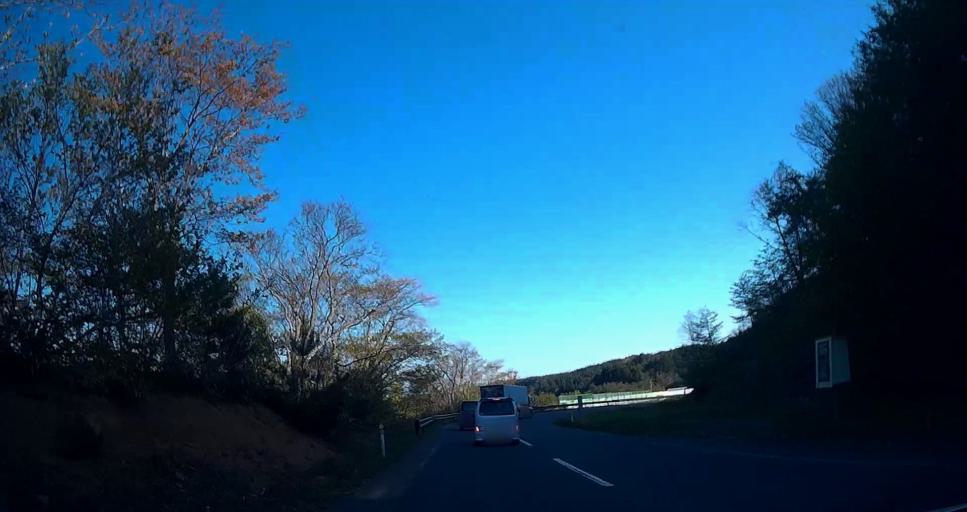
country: JP
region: Aomori
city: Mutsu
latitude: 41.4230
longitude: 141.1490
